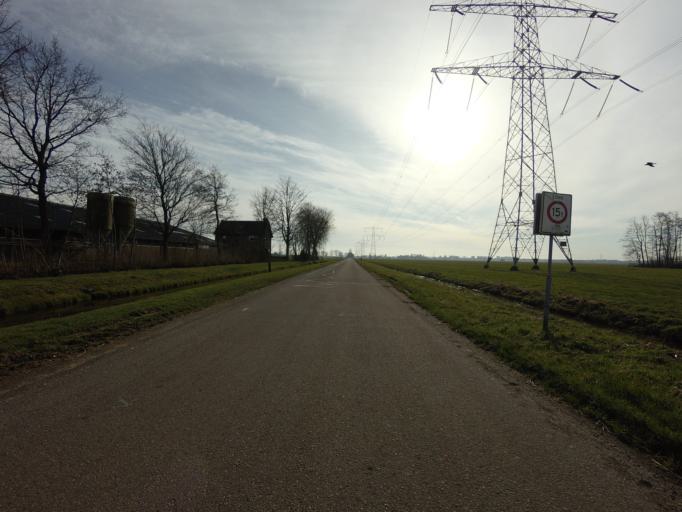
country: NL
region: South Holland
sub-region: Gemeente Sliedrecht
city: Sliedrecht
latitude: 51.8462
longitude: 4.8033
